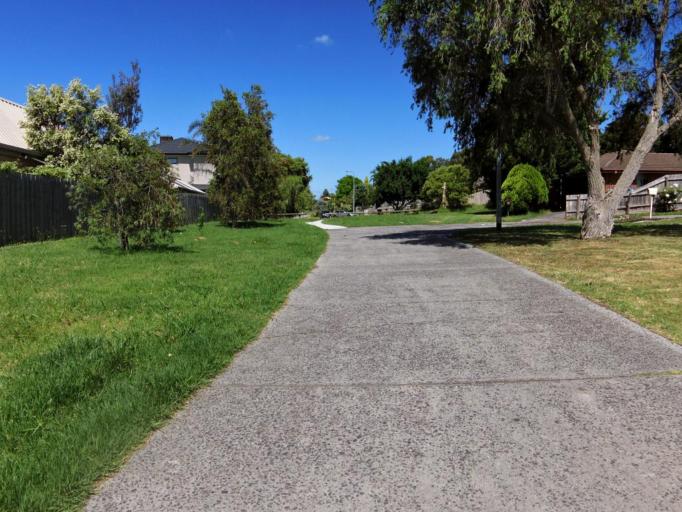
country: AU
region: Victoria
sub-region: Casey
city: Endeavour Hills
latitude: -37.9683
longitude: 145.2487
